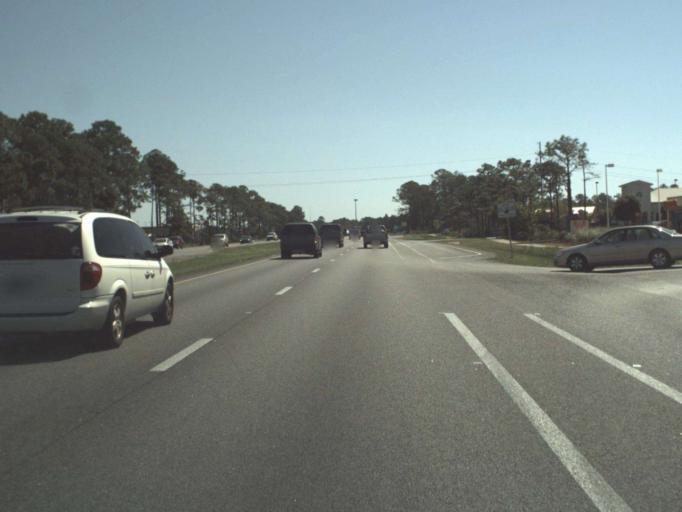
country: US
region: Florida
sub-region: Bay County
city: Panama City Beach
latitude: 30.2003
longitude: -85.8193
